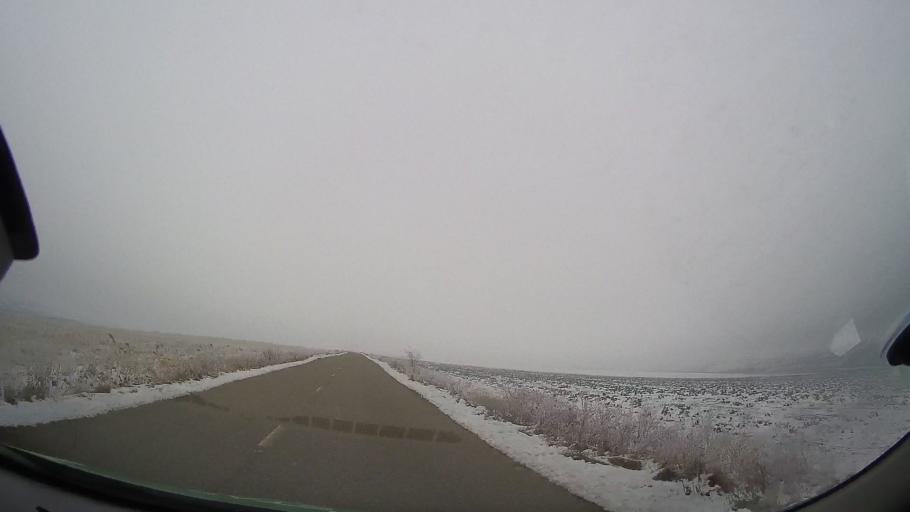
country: RO
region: Vaslui
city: Coroiesti
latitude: 46.2150
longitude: 27.4808
